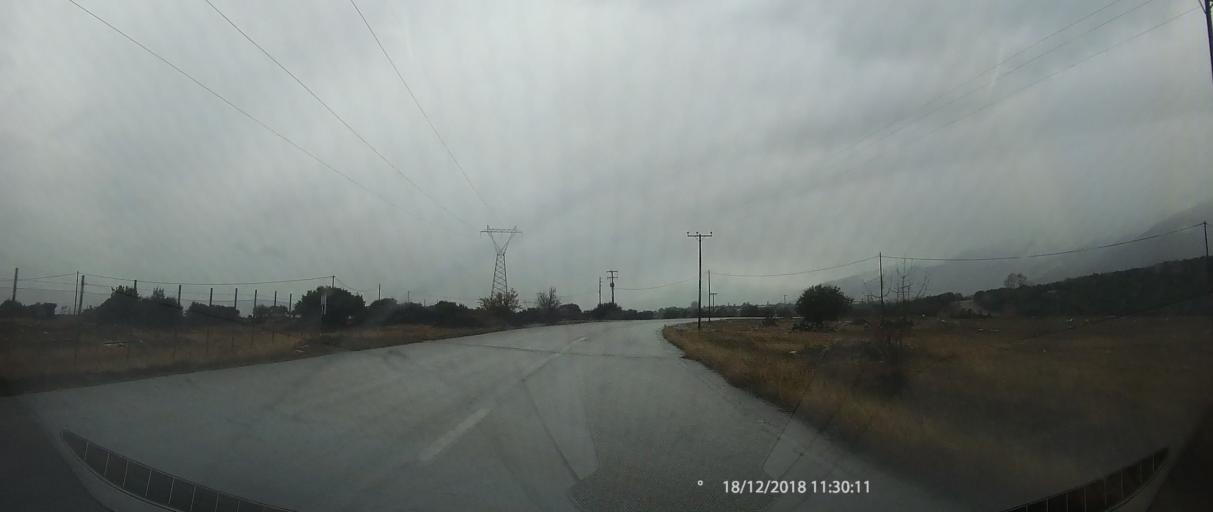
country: GR
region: Central Macedonia
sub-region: Nomos Pierias
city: Litochoro
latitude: 40.1261
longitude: 22.5228
